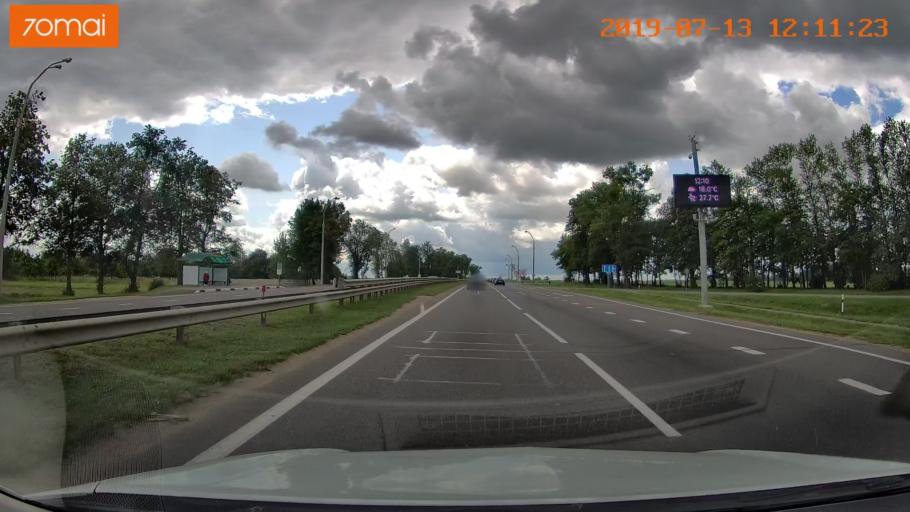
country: BY
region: Minsk
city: Yubilyeyny
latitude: 53.8064
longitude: 27.5293
